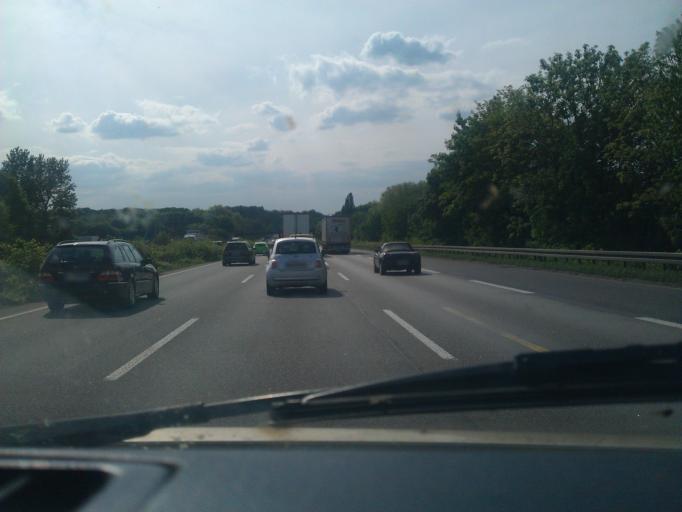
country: DE
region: North Rhine-Westphalia
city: Meiderich
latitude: 51.4785
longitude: 6.7195
